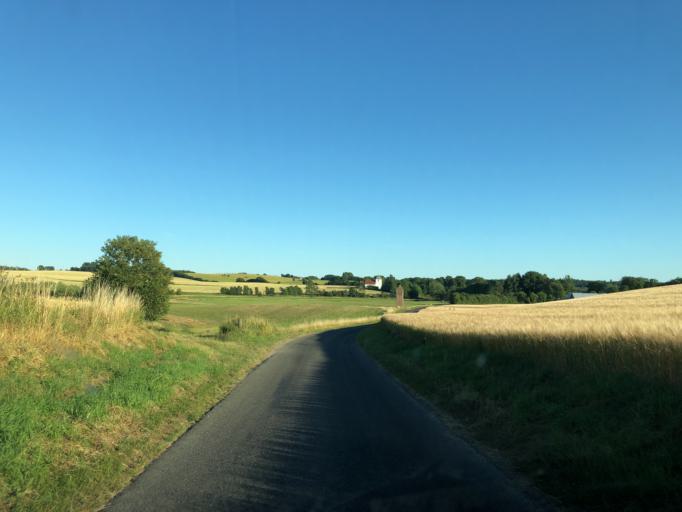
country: DK
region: Central Jutland
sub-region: Horsens Kommune
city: Horsens
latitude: 55.9365
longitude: 9.8663
